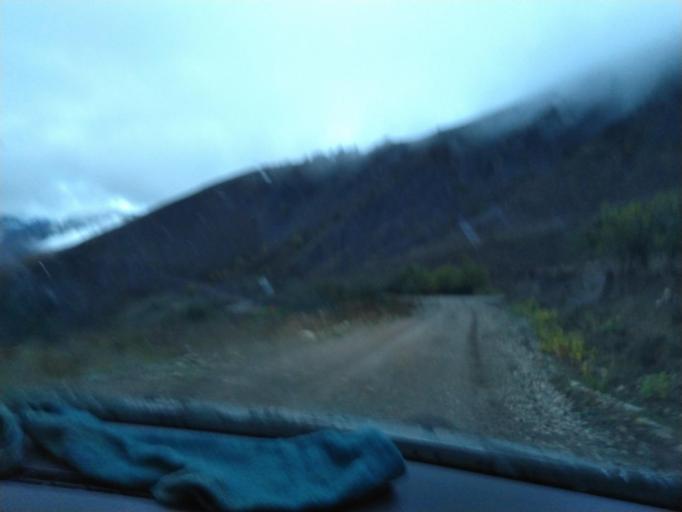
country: RU
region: North Ossetia
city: Tarskoye
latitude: 42.8232
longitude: 44.9708
